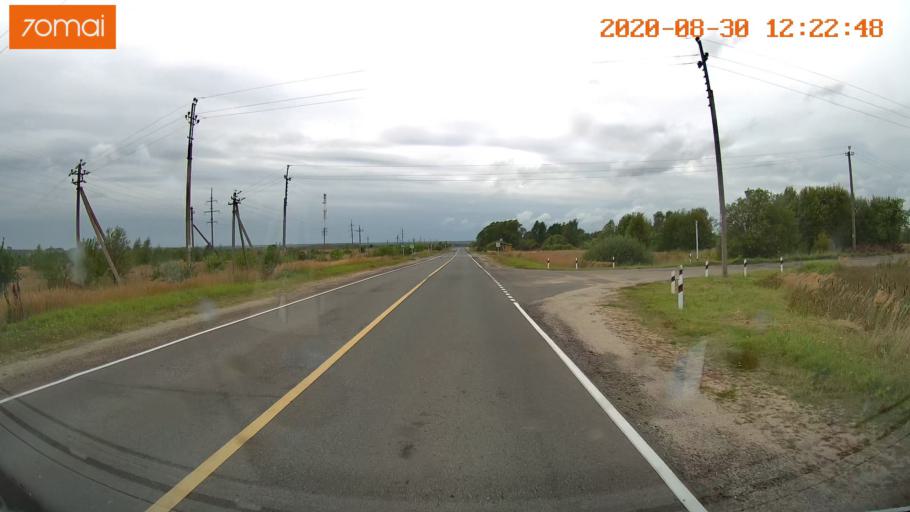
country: RU
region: Ivanovo
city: Yur'yevets
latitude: 57.3310
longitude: 42.8404
